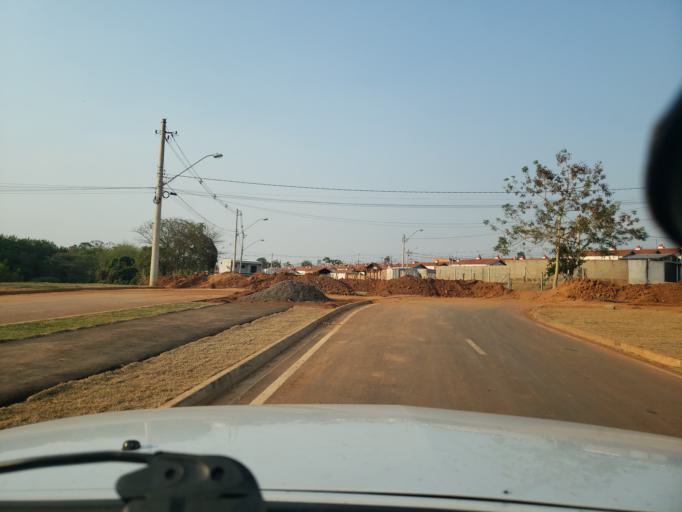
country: BR
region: Sao Paulo
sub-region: Moji-Guacu
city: Mogi-Gaucu
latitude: -22.3156
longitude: -46.9459
